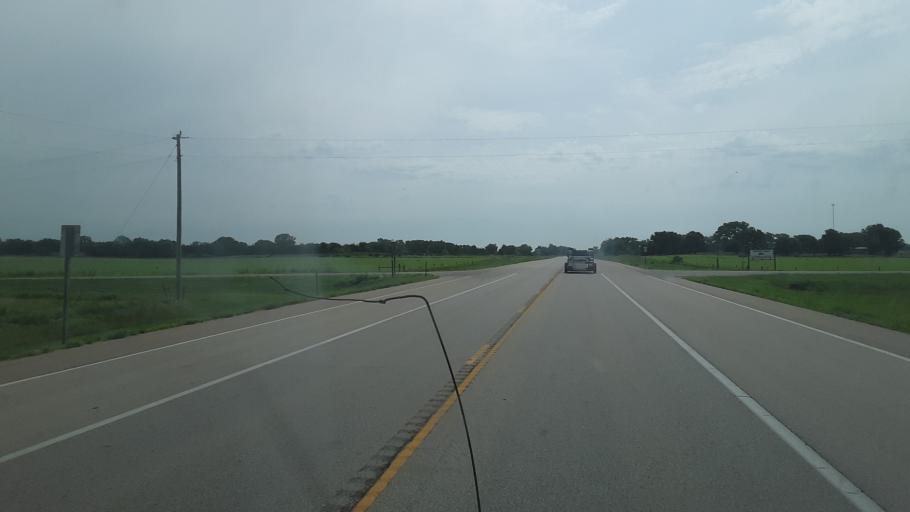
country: US
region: Kansas
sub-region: Rice County
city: Sterling
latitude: 37.9844
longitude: -98.3265
